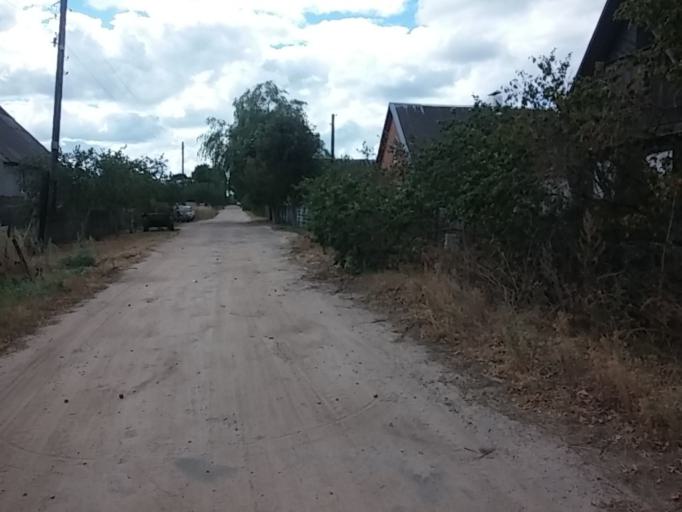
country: BY
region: Minsk
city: Chervyen'
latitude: 53.7818
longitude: 28.2697
